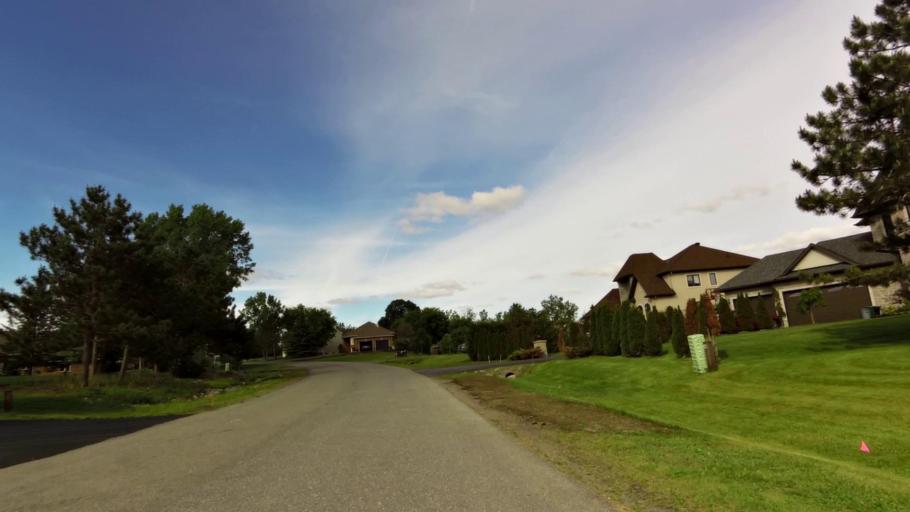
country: CA
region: Ontario
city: Ottawa
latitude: 45.2719
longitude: -75.5782
